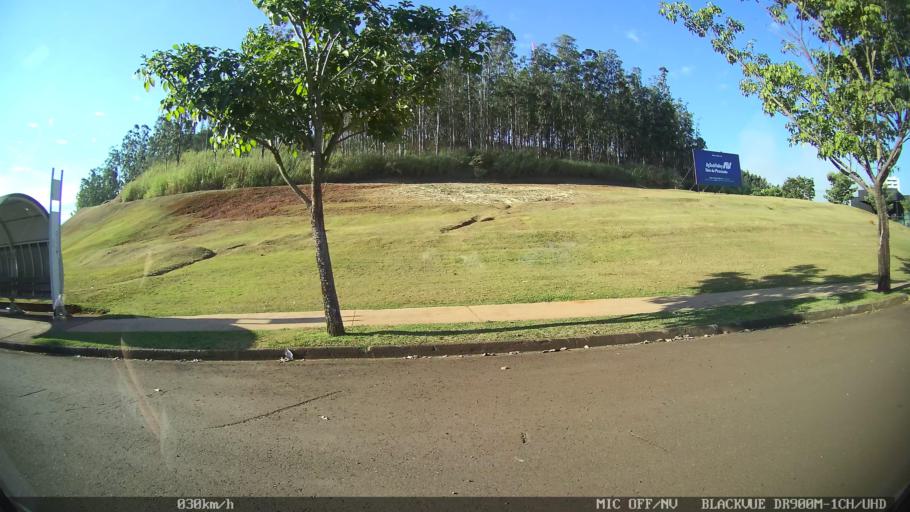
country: BR
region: Sao Paulo
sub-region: Piracicaba
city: Piracicaba
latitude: -22.6940
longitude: -47.6236
